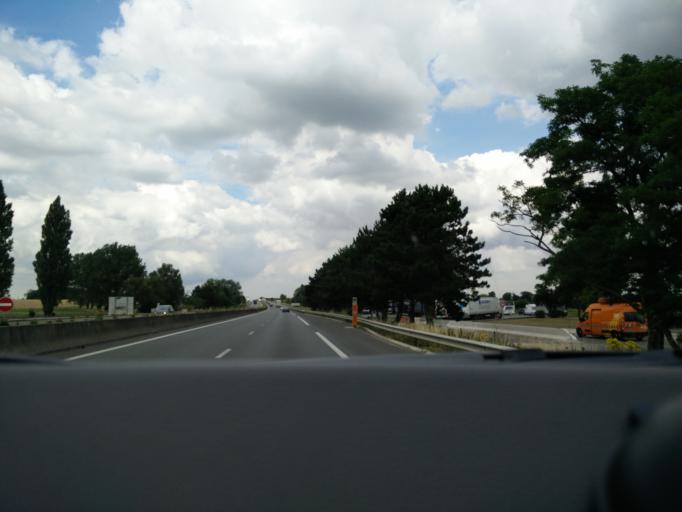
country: FR
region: Nord-Pas-de-Calais
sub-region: Departement du Nord
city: Steenvoorde
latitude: 50.8265
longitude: 2.5846
